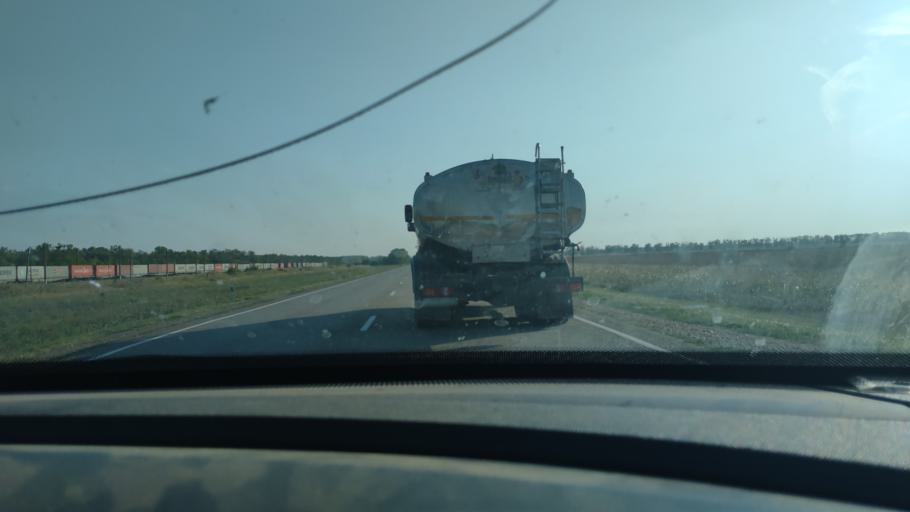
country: RU
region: Krasnodarskiy
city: Starominskaya
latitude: 46.4373
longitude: 39.0206
